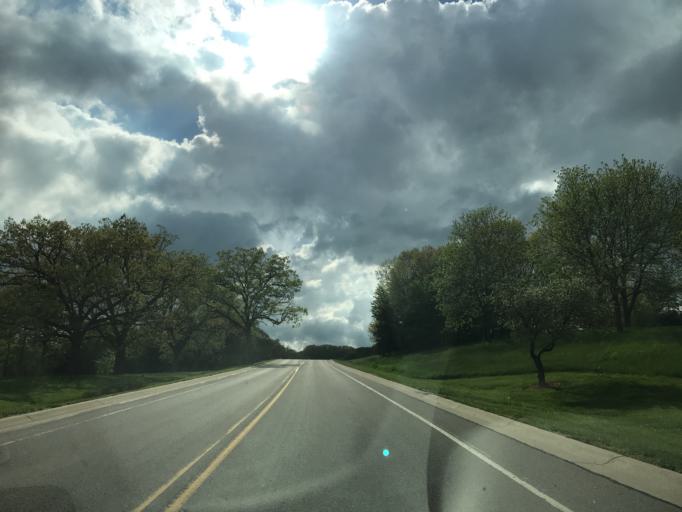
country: US
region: Michigan
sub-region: Oakland County
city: Milford
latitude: 42.5501
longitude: -83.6348
